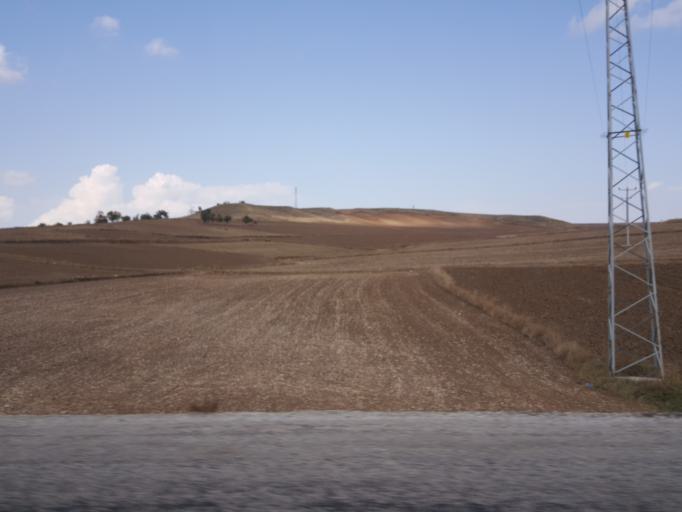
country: TR
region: Corum
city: Alaca
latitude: 40.1575
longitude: 34.7090
